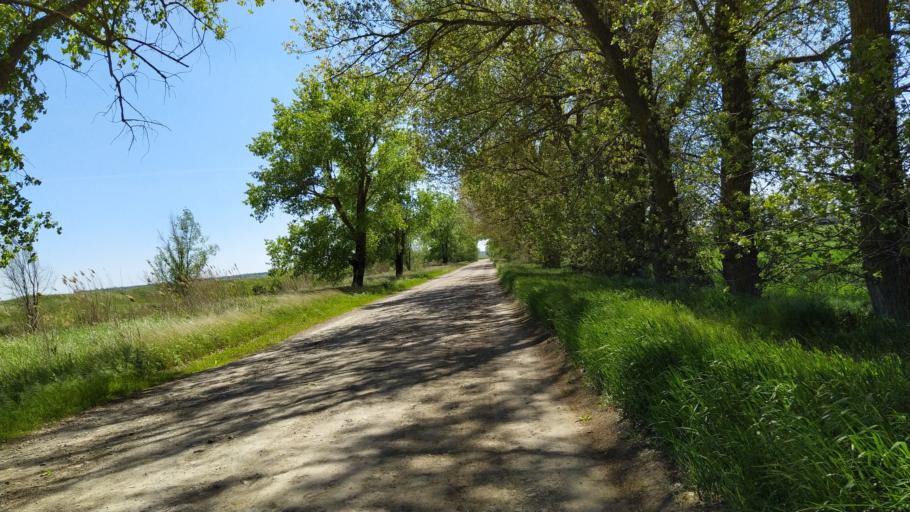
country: RU
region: Rostov
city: Kuleshovka
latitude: 47.0604
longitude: 39.6250
